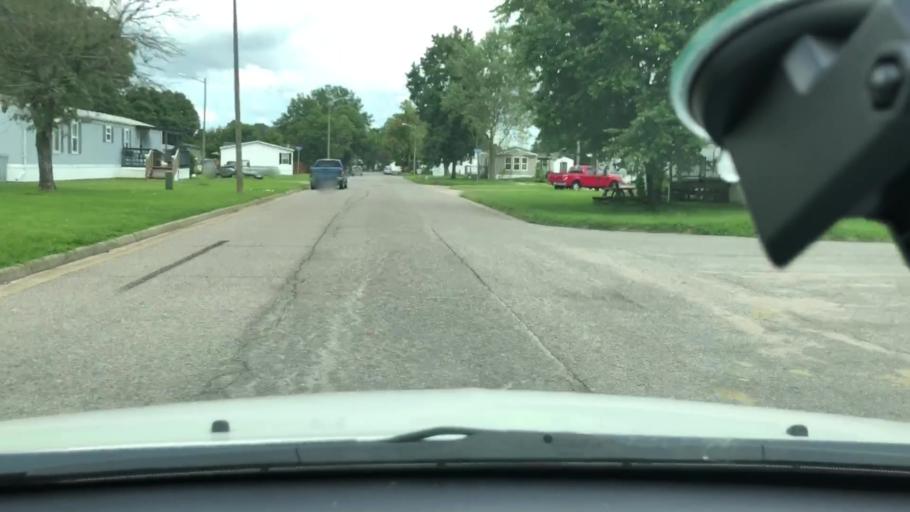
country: US
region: Virginia
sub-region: City of Chesapeake
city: Chesapeake
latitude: 36.7771
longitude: -76.2776
